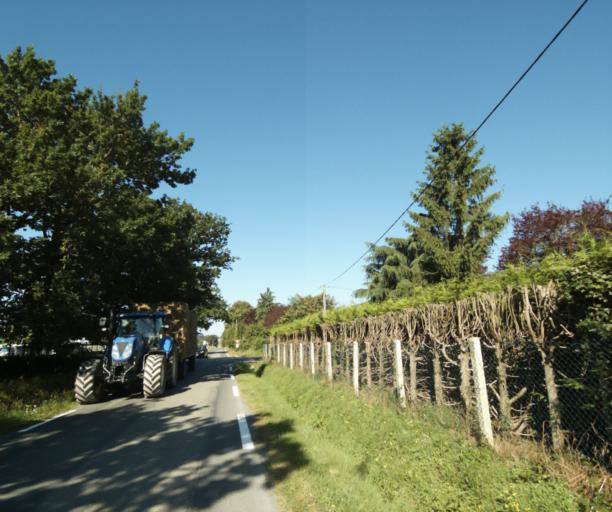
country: FR
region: Pays de la Loire
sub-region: Departement de la Mayenne
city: Laval
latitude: 48.0386
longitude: -0.7376
